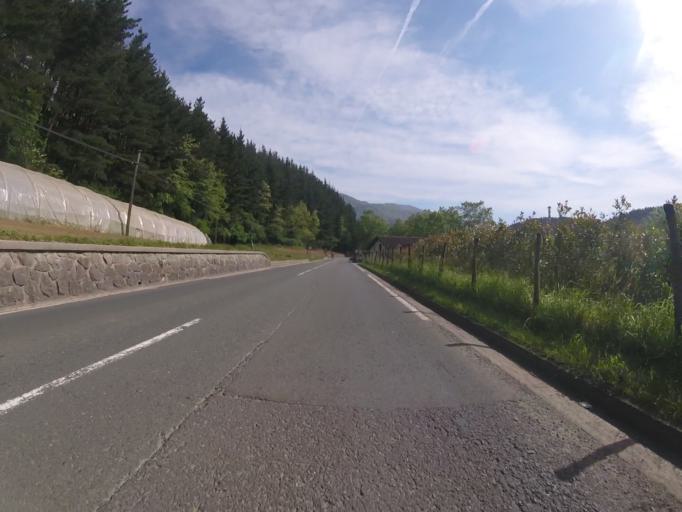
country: ES
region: Basque Country
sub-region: Provincia de Guipuzcoa
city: Azkoitia
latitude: 43.1682
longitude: -2.3278
